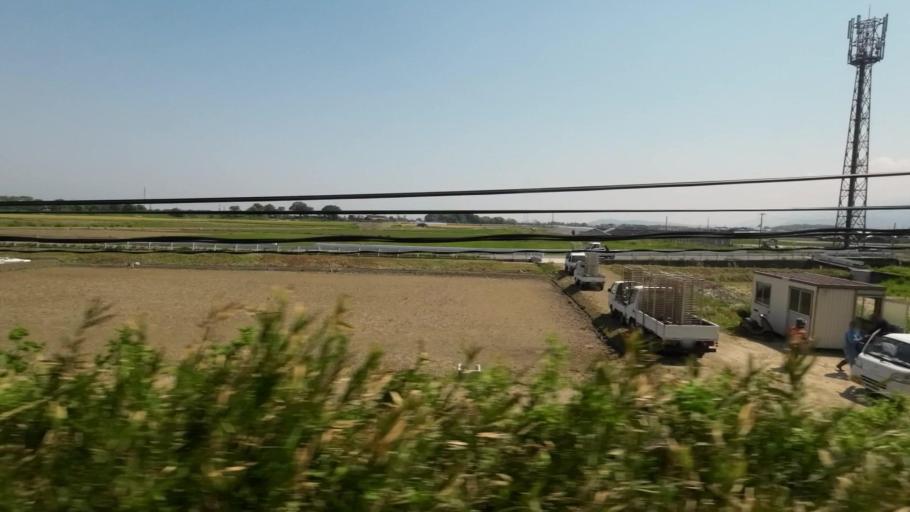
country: JP
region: Ehime
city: Saijo
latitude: 33.9005
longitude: 133.1007
